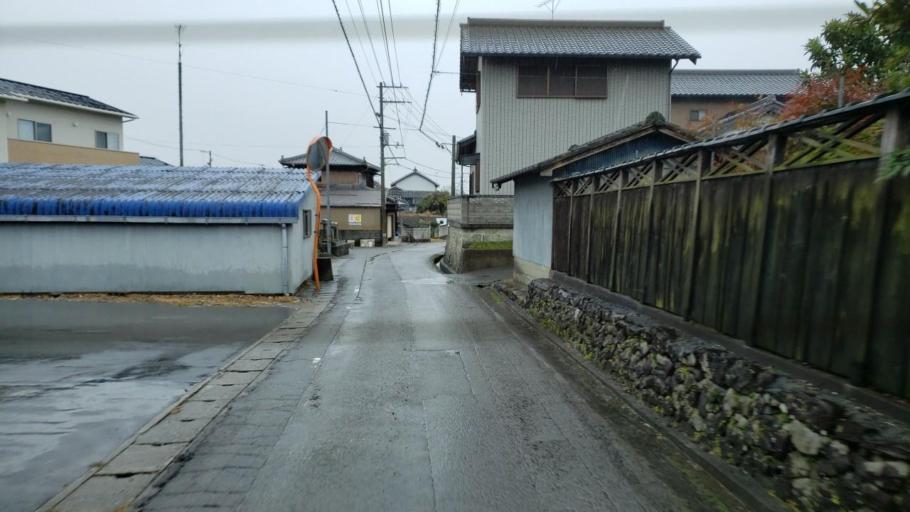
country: JP
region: Tokushima
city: Wakimachi
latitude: 34.0775
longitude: 134.2450
